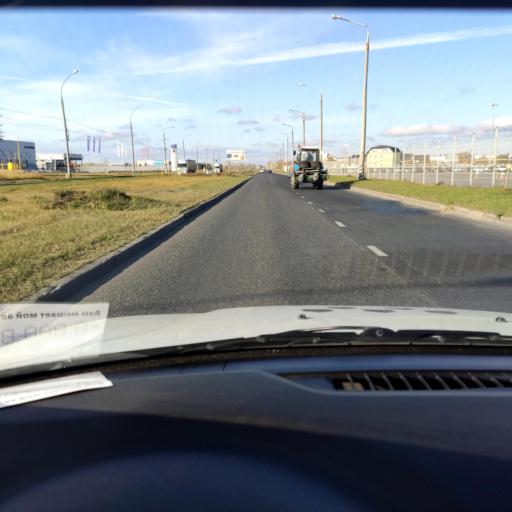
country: RU
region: Samara
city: Tol'yatti
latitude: 53.5565
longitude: 49.3433
